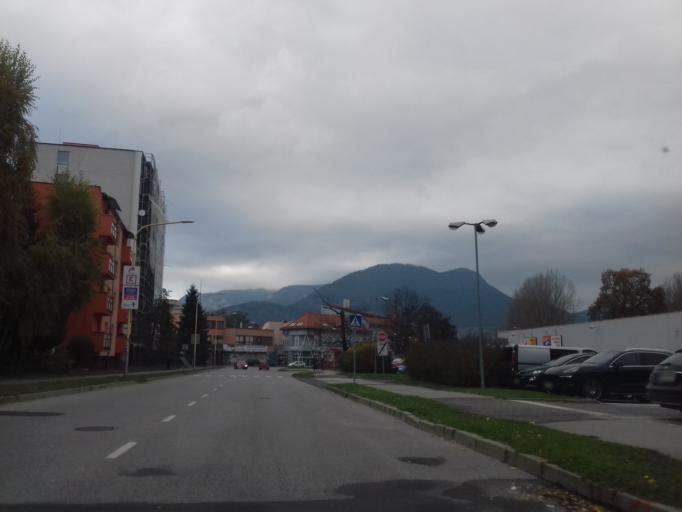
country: SK
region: Zilinsky
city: Ruzomberok
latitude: 49.0779
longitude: 19.3040
